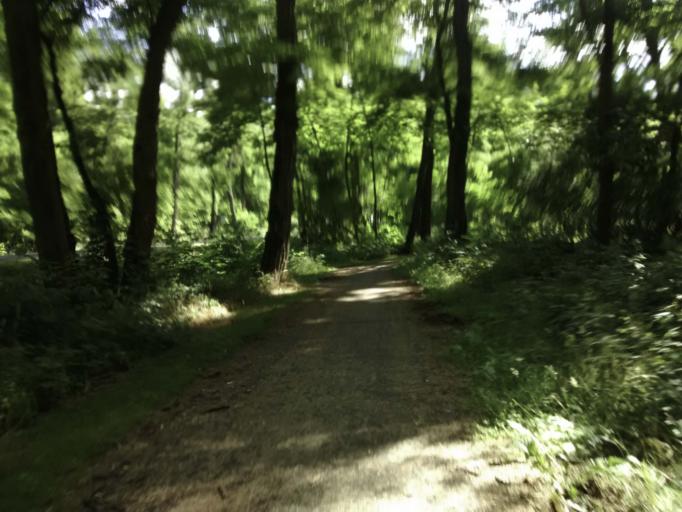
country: DE
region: Saxony-Anhalt
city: Tangerhutte
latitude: 52.3963
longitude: 11.9332
